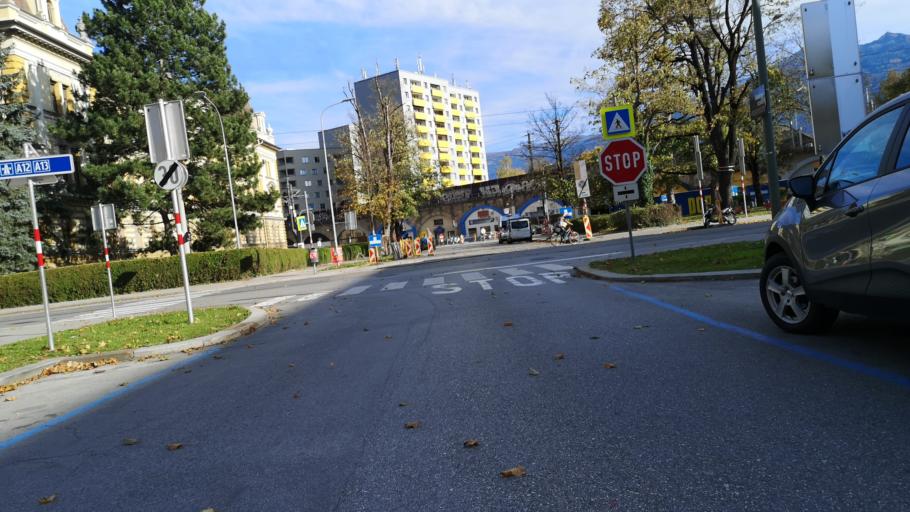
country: AT
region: Tyrol
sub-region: Innsbruck Stadt
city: Innsbruck
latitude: 47.2724
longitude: 11.4046
